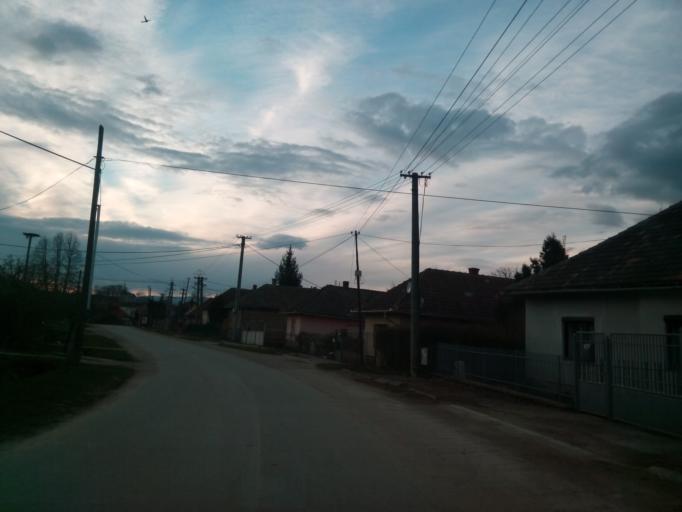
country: SK
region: Kosicky
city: Moldava nad Bodvou
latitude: 48.5537
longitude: 20.9732
